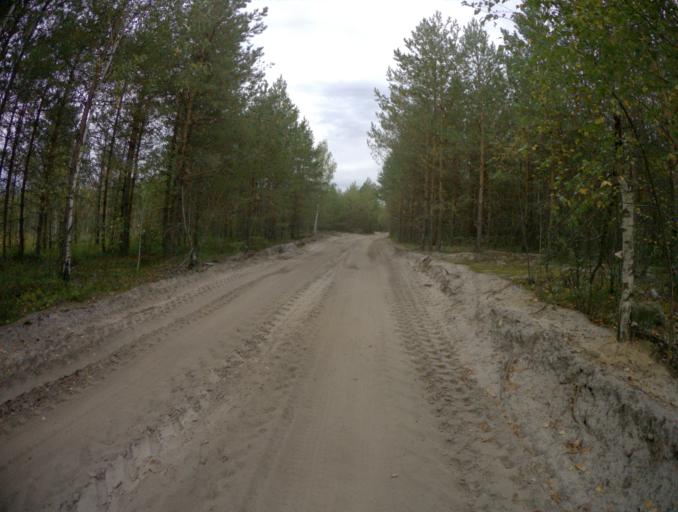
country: RU
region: Vladimir
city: Vorsha
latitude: 55.8904
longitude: 40.1834
